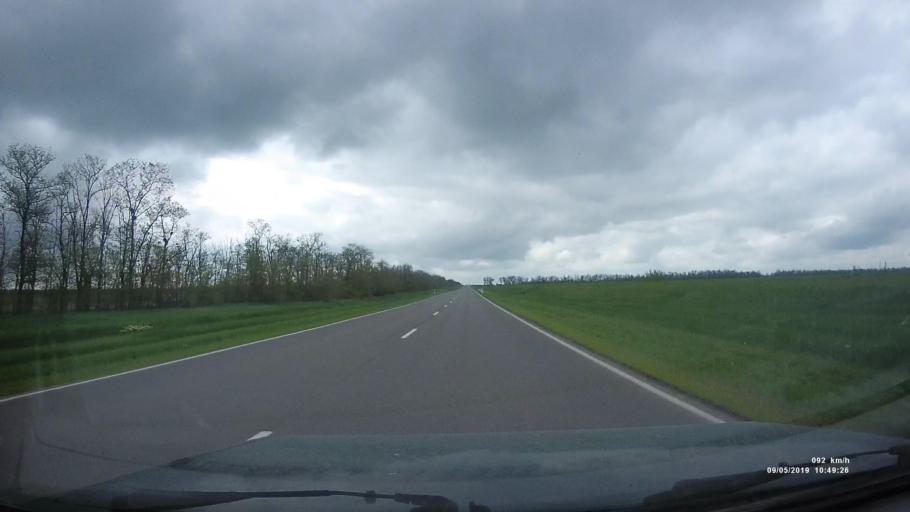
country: RU
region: Rostov
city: Peshkovo
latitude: 46.9424
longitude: 39.3570
